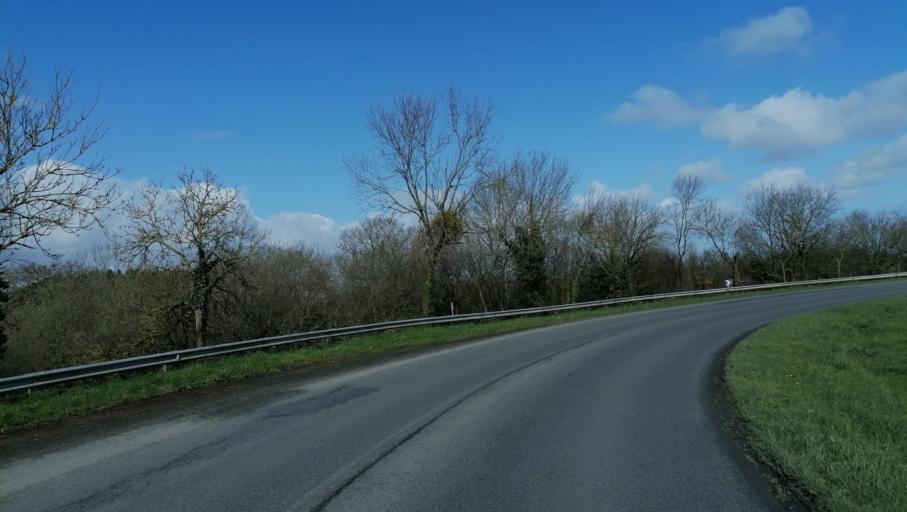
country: FR
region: Brittany
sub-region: Departement des Cotes-d'Armor
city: Tremuson
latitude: 48.5312
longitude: -2.8589
